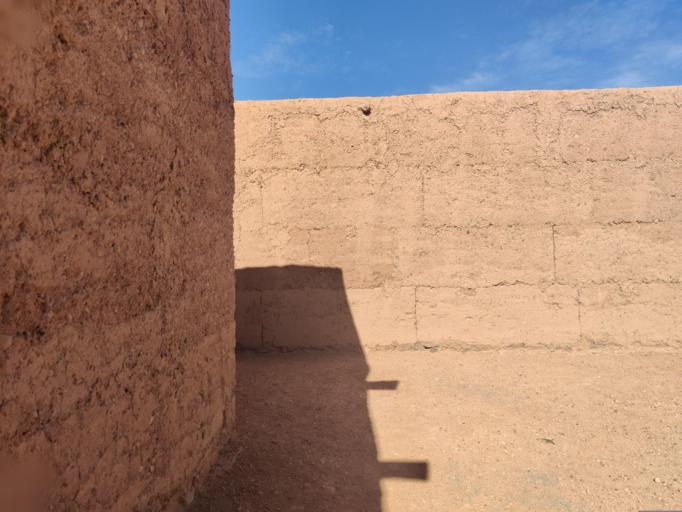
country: MA
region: Souss-Massa-Draa
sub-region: Ouarzazate
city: Ouarzazat
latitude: 30.9527
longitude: -6.9876
